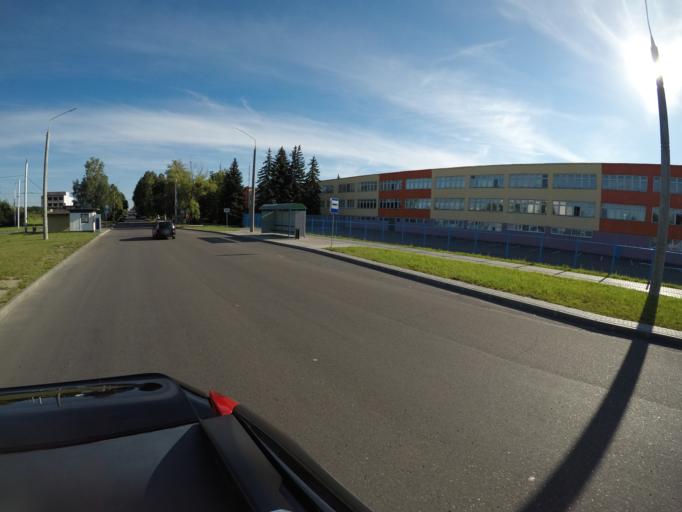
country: BY
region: Grodnenskaya
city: Hrodna
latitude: 53.7147
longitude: 23.8253
